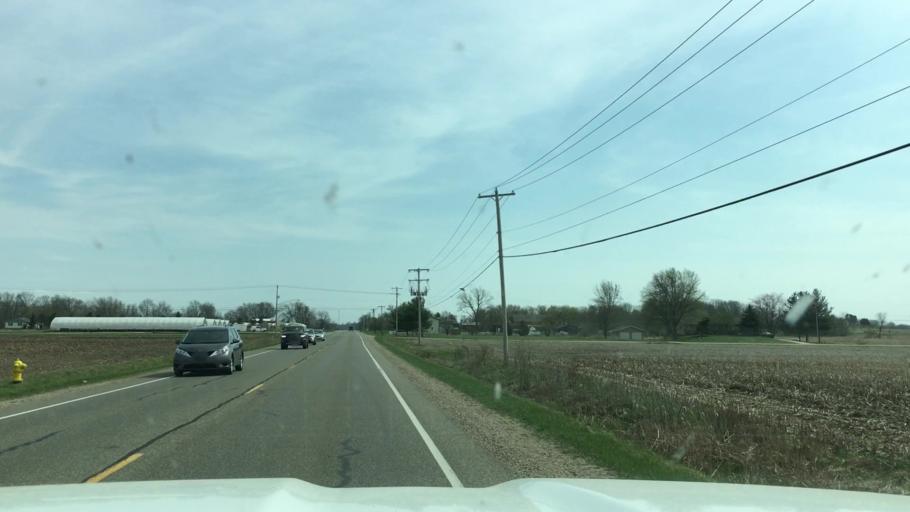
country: US
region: Michigan
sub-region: Ottawa County
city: Hudsonville
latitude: 42.8723
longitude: -85.9011
